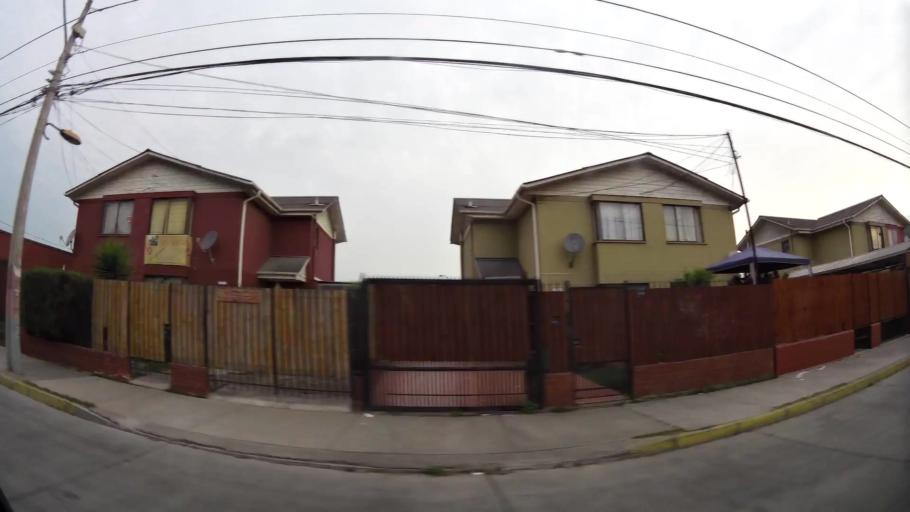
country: CL
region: Santiago Metropolitan
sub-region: Provincia de Santiago
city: Lo Prado
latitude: -33.5249
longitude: -70.7896
